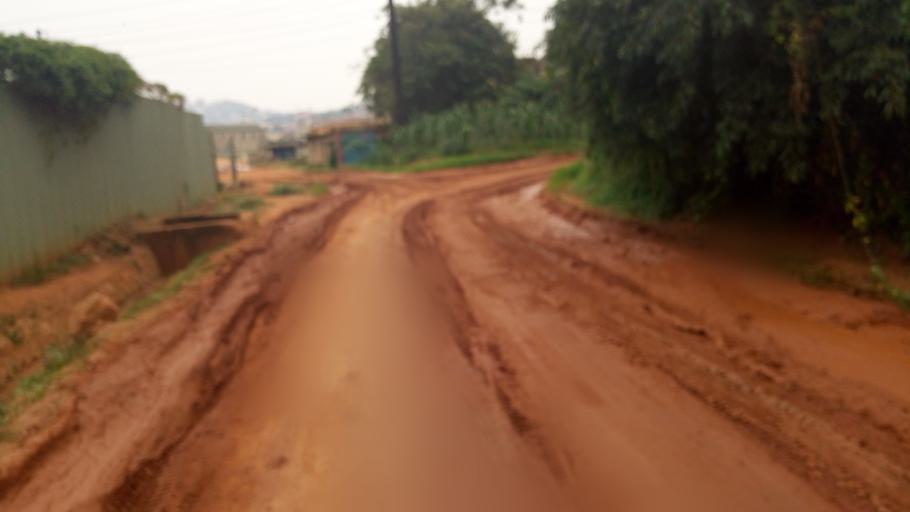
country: UG
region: Central Region
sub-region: Kampala District
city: Kampala
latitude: 0.3201
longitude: 32.6083
